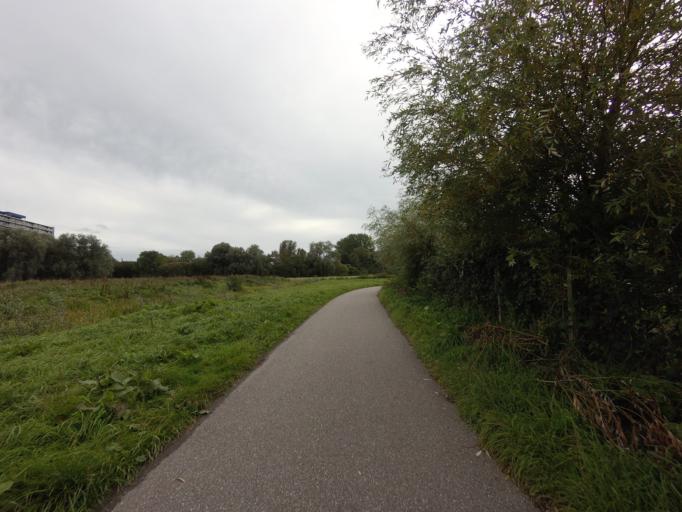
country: NL
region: Friesland
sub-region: Gemeente Leeuwarden
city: Bilgaard
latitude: 53.2194
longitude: 5.7935
